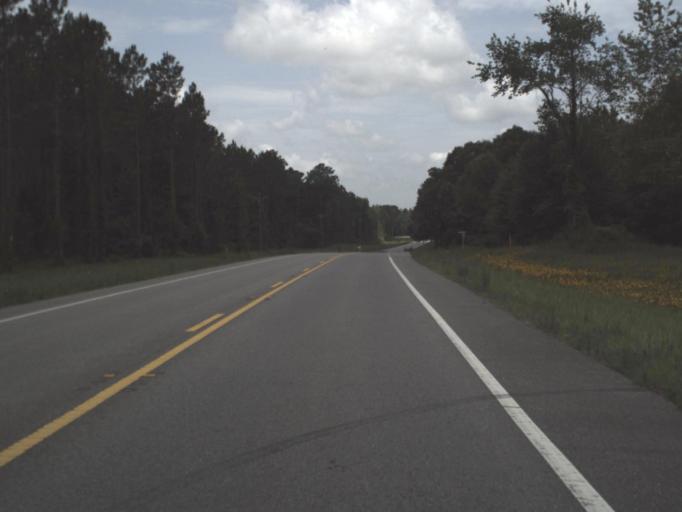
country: US
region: Florida
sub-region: Madison County
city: Madison
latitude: 30.4886
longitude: -83.4991
